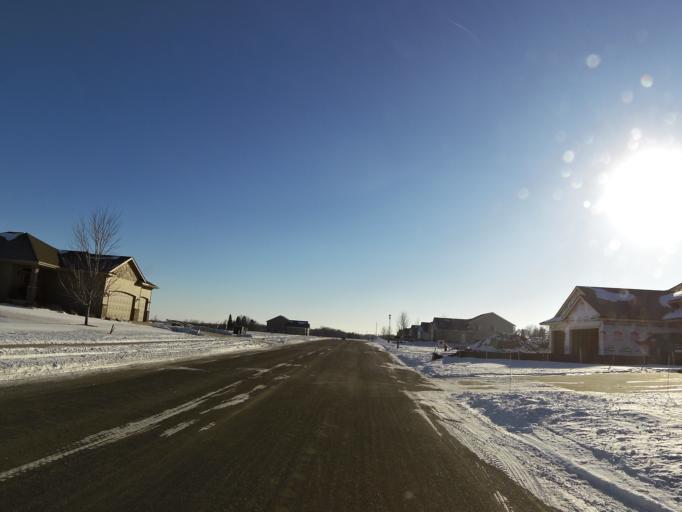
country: US
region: Minnesota
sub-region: Le Sueur County
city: New Prague
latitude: 44.5475
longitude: -93.6017
